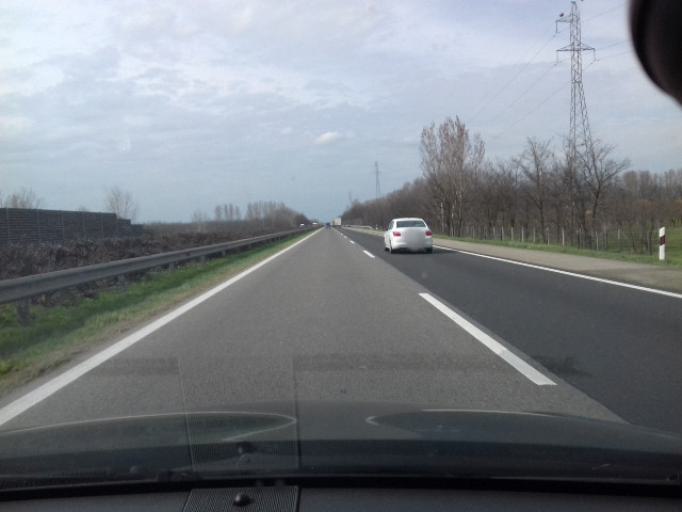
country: HU
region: Pest
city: Taborfalva
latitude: 47.0808
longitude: 19.5286
